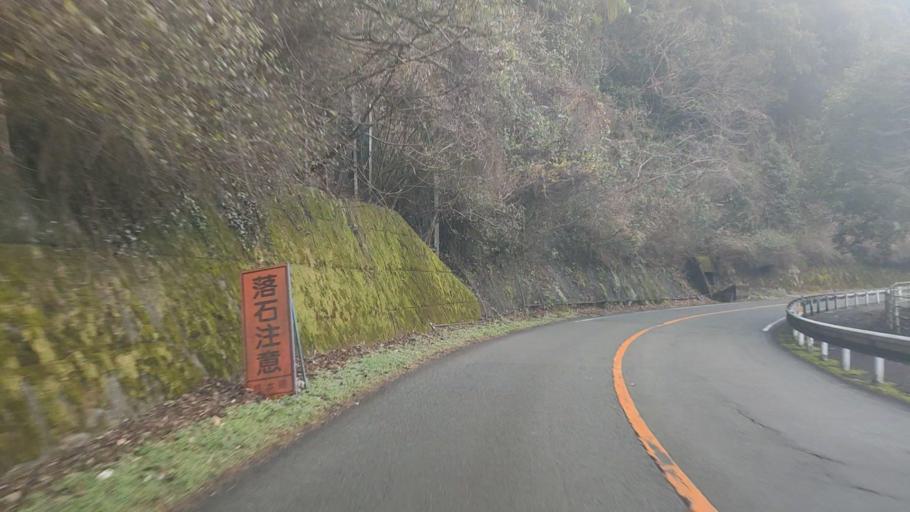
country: JP
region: Kumamoto
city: Hitoyoshi
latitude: 32.3001
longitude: 130.8466
